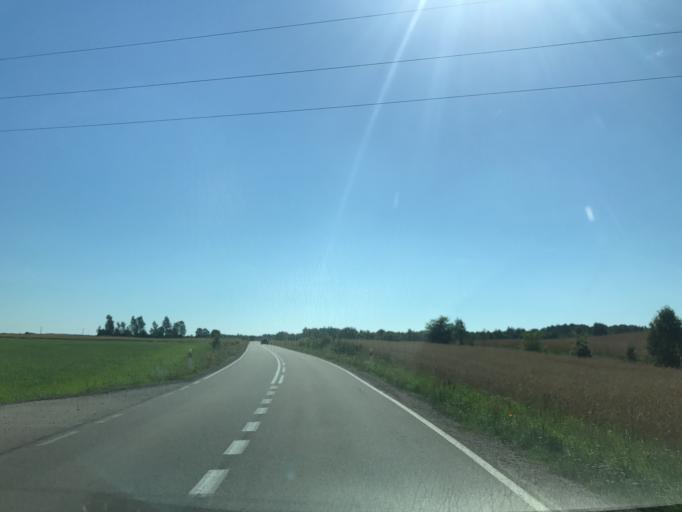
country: PL
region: Pomeranian Voivodeship
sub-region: Powiat leborski
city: Cewice
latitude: 54.3392
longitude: 17.6916
